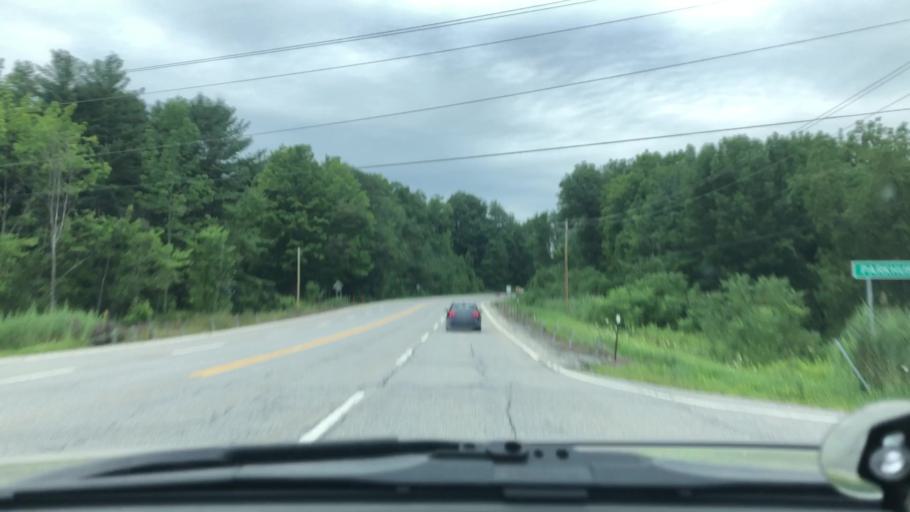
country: US
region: New York
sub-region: Saratoga County
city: Saratoga Springs
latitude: 43.1802
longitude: -73.7483
